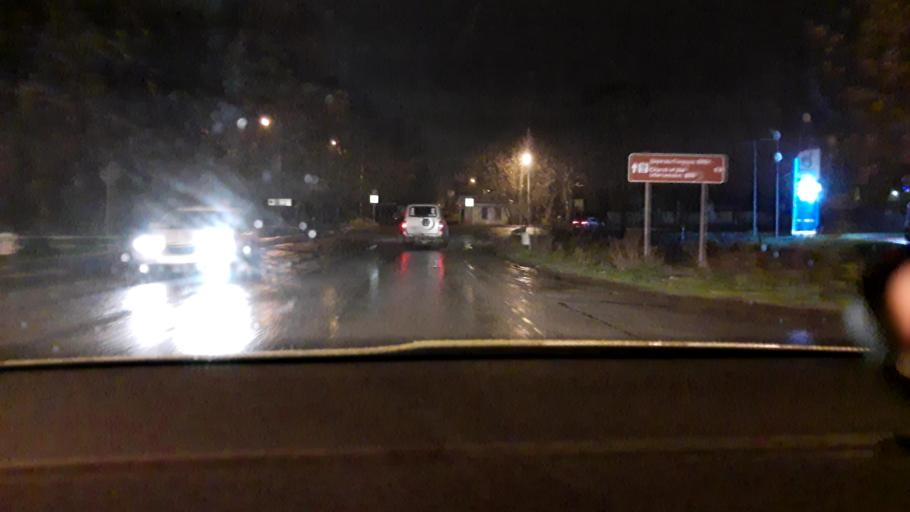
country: RU
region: Moskovskaya
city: Shchelkovo
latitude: 55.9274
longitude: 37.9827
